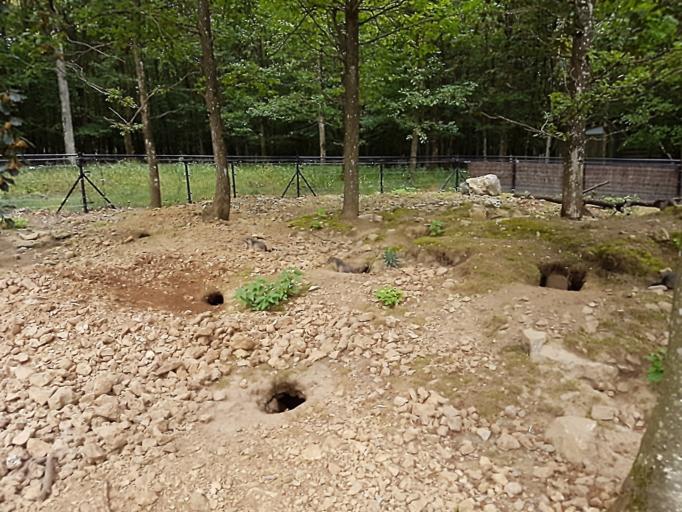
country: BE
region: Wallonia
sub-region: Province du Luxembourg
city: Tellin
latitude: 50.1171
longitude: 5.1960
